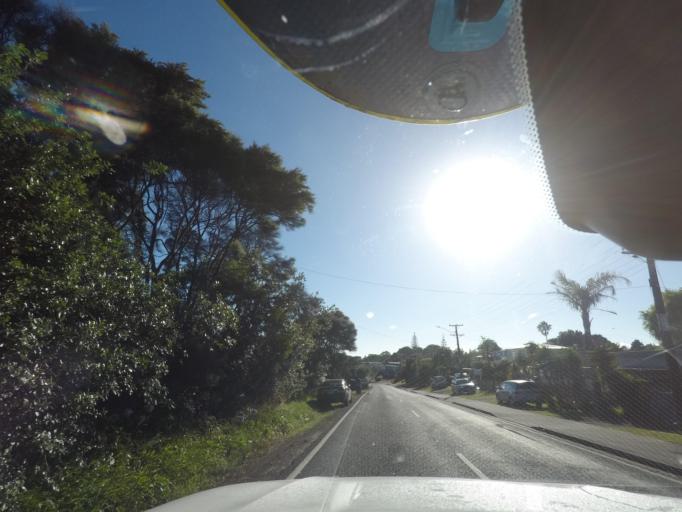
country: NZ
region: Auckland
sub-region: Auckland
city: Parakai
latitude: -36.5704
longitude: 174.3744
